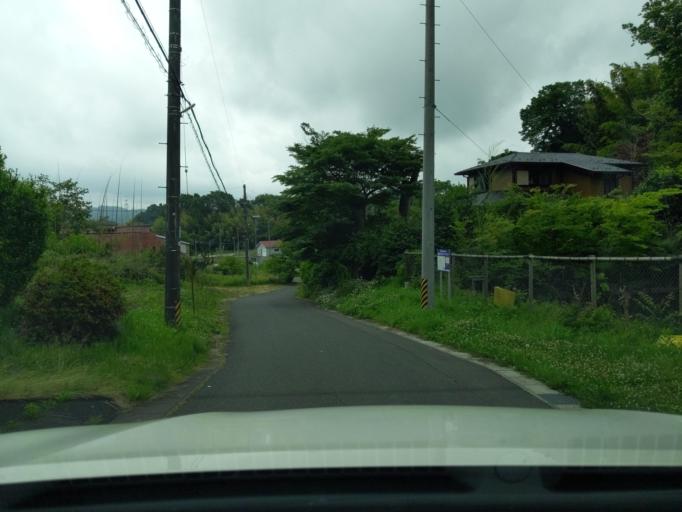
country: JP
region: Fukushima
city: Miharu
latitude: 37.4046
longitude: 140.4449
